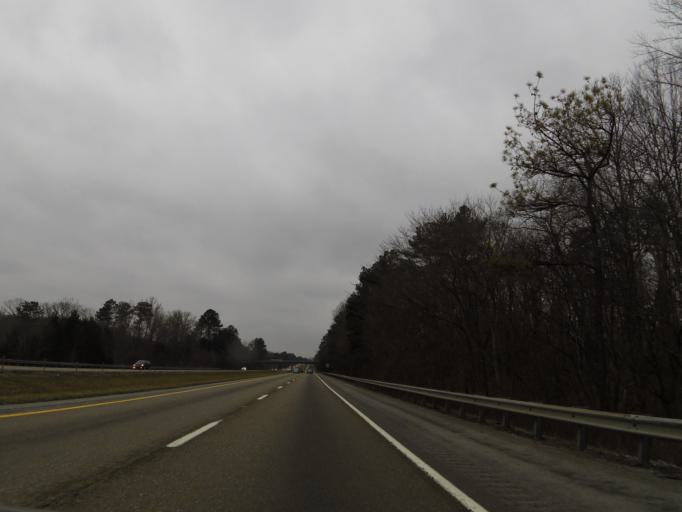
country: US
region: Tennessee
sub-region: Roane County
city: Kingston
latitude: 35.8682
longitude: -84.3832
